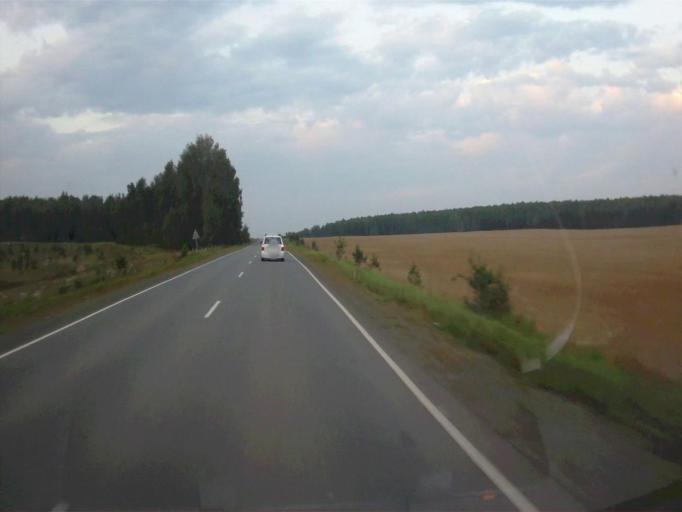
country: RU
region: Chelyabinsk
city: Chebarkul'
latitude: 55.1662
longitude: 60.4471
